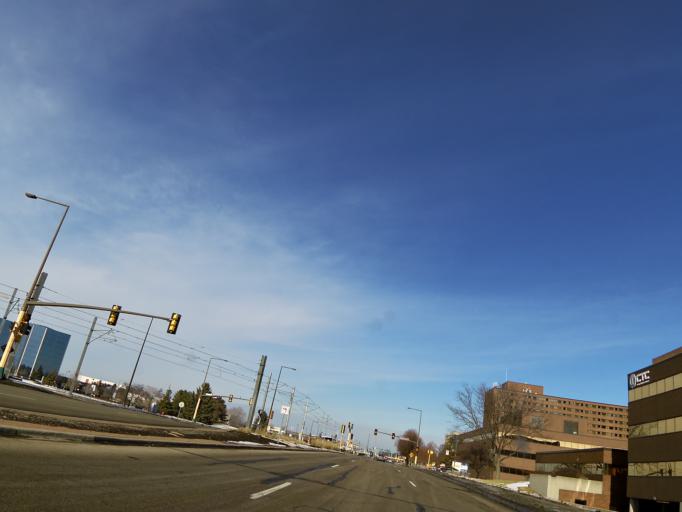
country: US
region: Minnesota
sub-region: Hennepin County
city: Richfield
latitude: 44.8562
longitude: -93.2230
